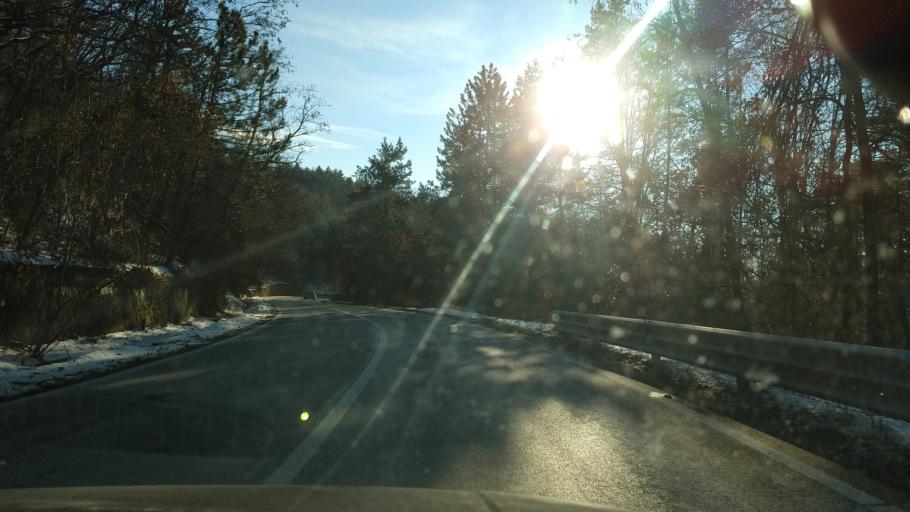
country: RO
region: Bacau
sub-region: Comuna Luizi-Calugara
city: Luizi-Calugara
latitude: 46.4951
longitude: 26.7942
